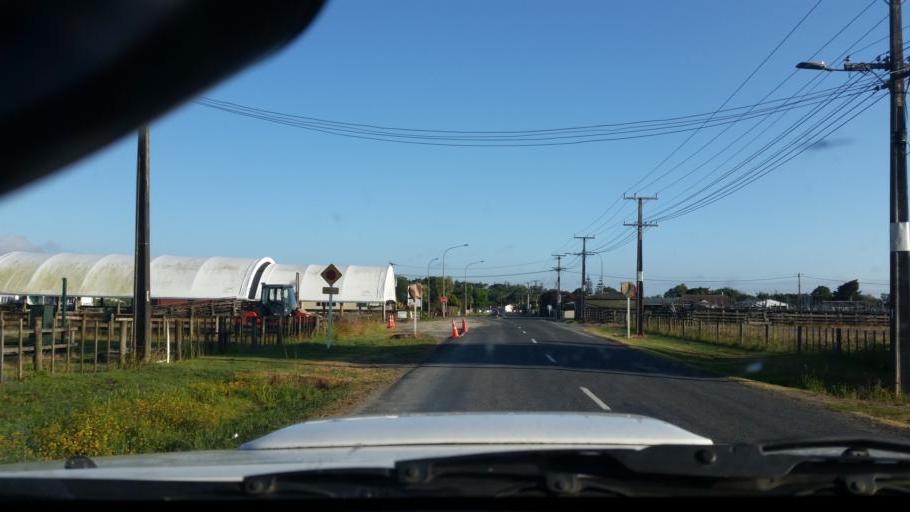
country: NZ
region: Northland
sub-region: Kaipara District
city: Dargaville
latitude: -35.9523
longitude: 173.8630
